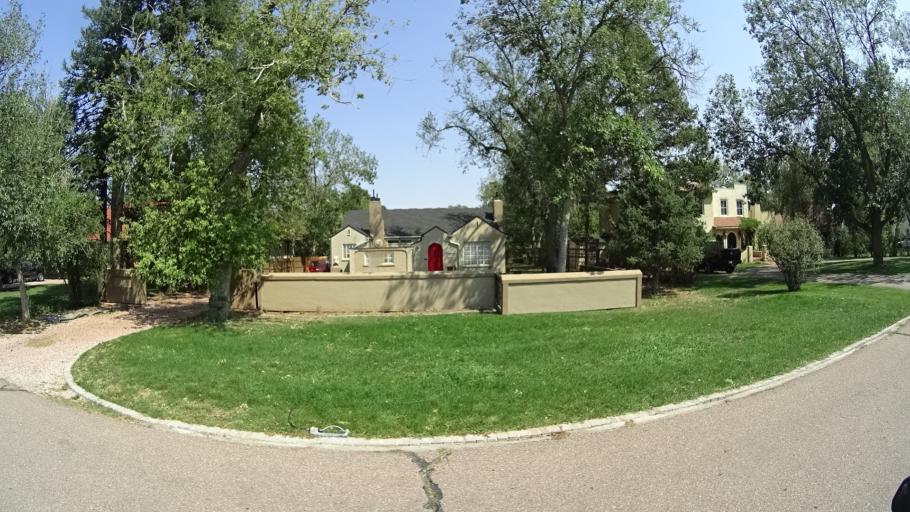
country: US
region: Colorado
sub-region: El Paso County
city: Colorado Springs
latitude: 38.7951
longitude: -104.8483
